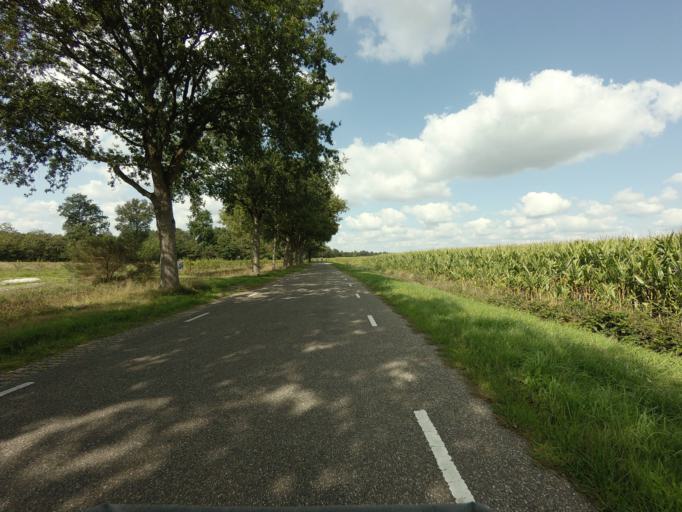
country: NL
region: Drenthe
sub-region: Gemeente Westerveld
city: Dwingeloo
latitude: 52.8593
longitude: 6.3891
